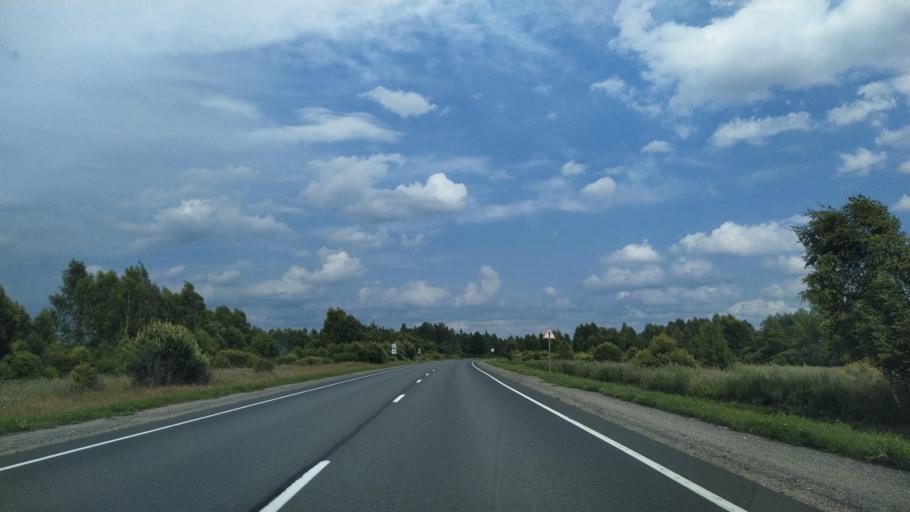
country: RU
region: Pskov
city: Porkhov
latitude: 57.9760
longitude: 29.7075
